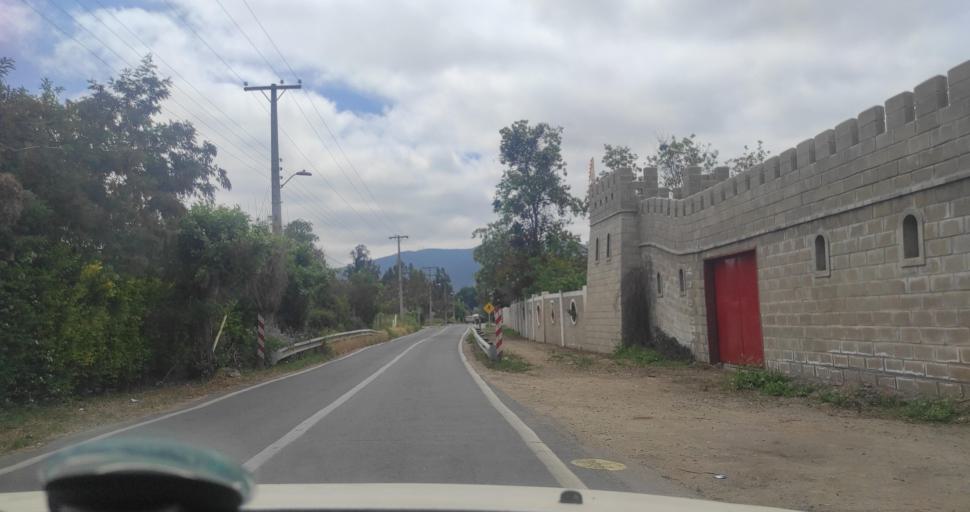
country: CL
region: Valparaiso
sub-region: Provincia de Marga Marga
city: Limache
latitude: -33.0187
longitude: -71.2425
